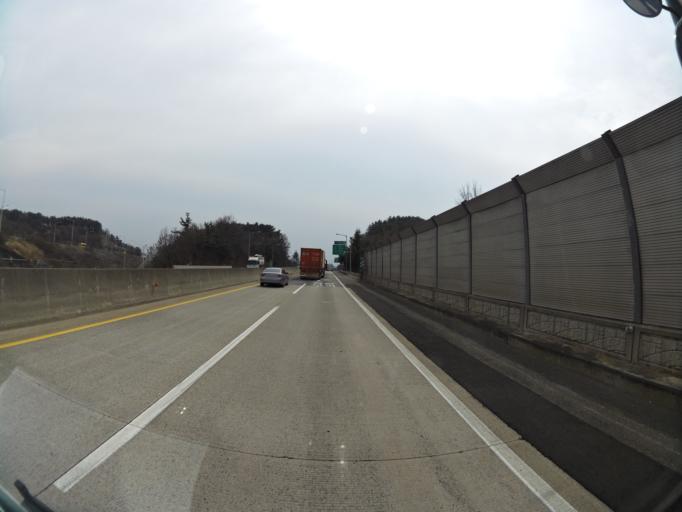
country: KR
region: Gyeongsangnam-do
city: Changnyeong
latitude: 35.4596
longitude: 128.5123
